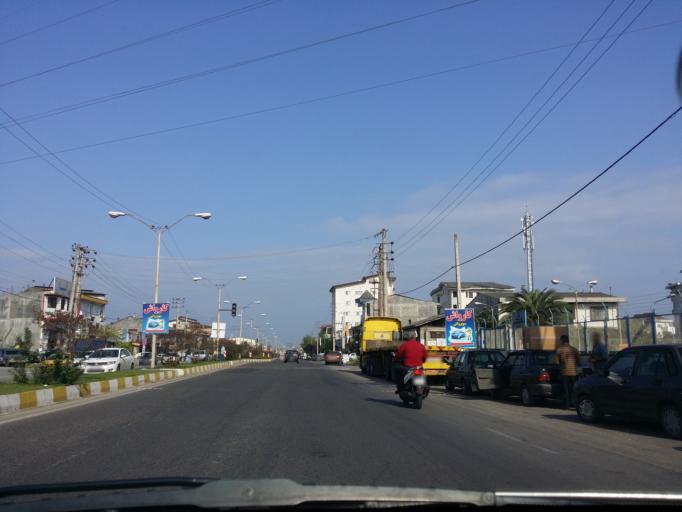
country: IR
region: Mazandaran
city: Chalus
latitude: 36.6709
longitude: 51.4075
